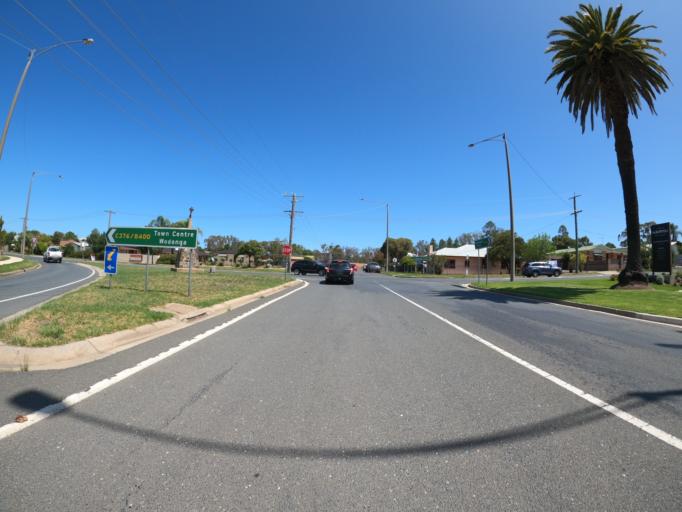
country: AU
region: New South Wales
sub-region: Corowa Shire
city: Corowa
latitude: -36.0521
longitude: 146.4550
